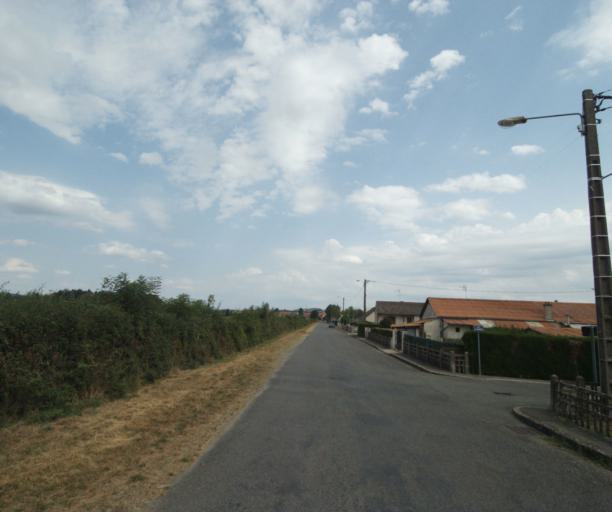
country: FR
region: Bourgogne
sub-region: Departement de Saone-et-Loire
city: Gueugnon
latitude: 46.6089
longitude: 4.0541
